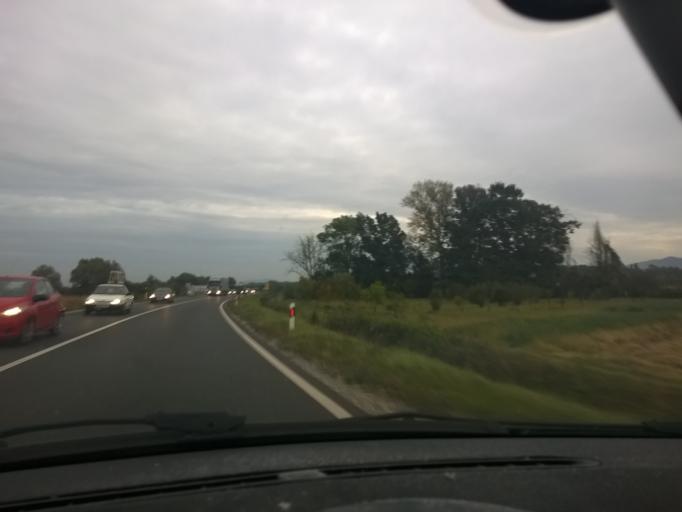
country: HR
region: Zagrebacka
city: Pojatno
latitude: 45.9079
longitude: 15.8136
